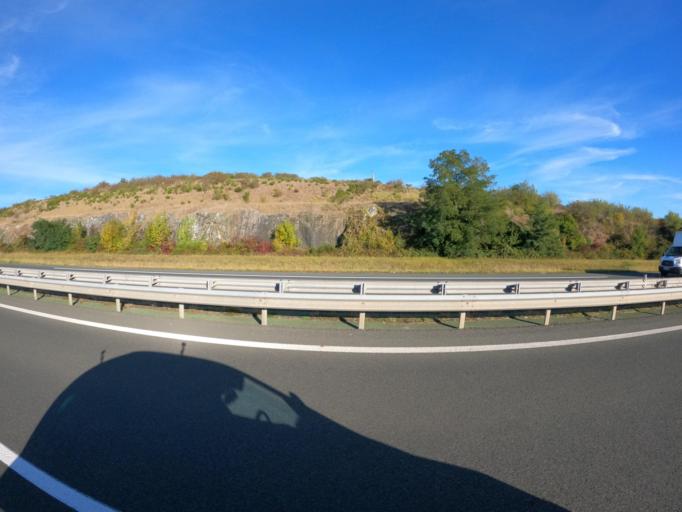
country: FR
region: Pays de la Loire
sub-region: Departement de Maine-et-Loire
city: Beaulieu-sur-Layon
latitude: 47.3140
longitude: -0.6068
